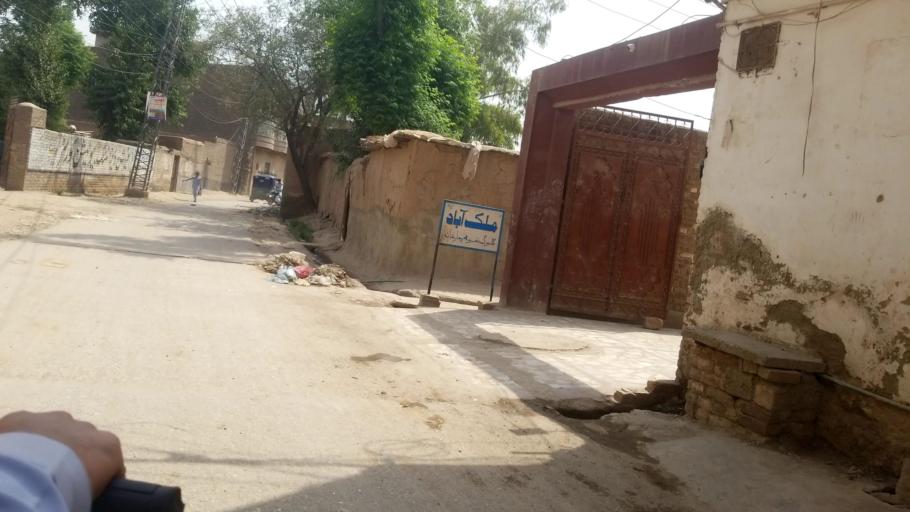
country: PK
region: Khyber Pakhtunkhwa
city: Peshawar
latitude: 33.9840
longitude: 71.5386
